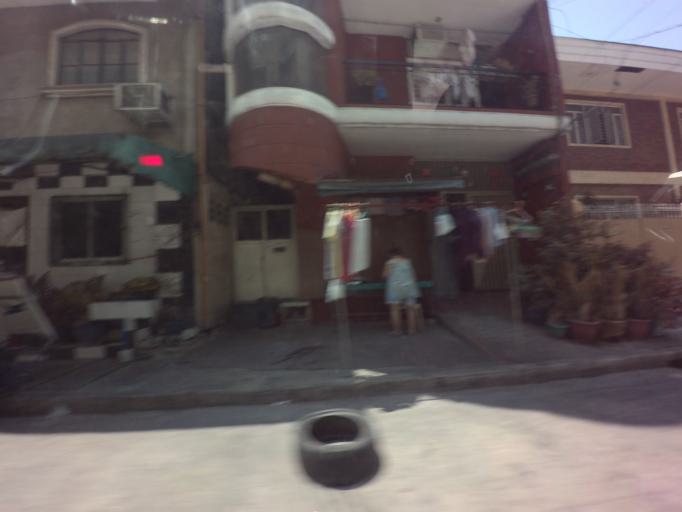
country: PH
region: Metro Manila
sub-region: Makati City
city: Makati City
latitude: 14.5632
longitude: 121.0011
